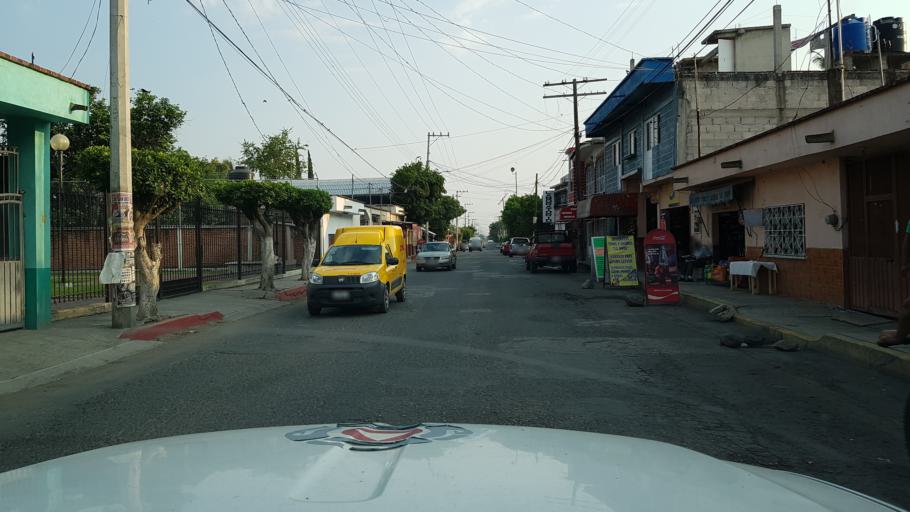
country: MX
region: Morelos
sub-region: Ayala
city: Ciudad Ayala
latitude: 18.7796
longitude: -98.9807
